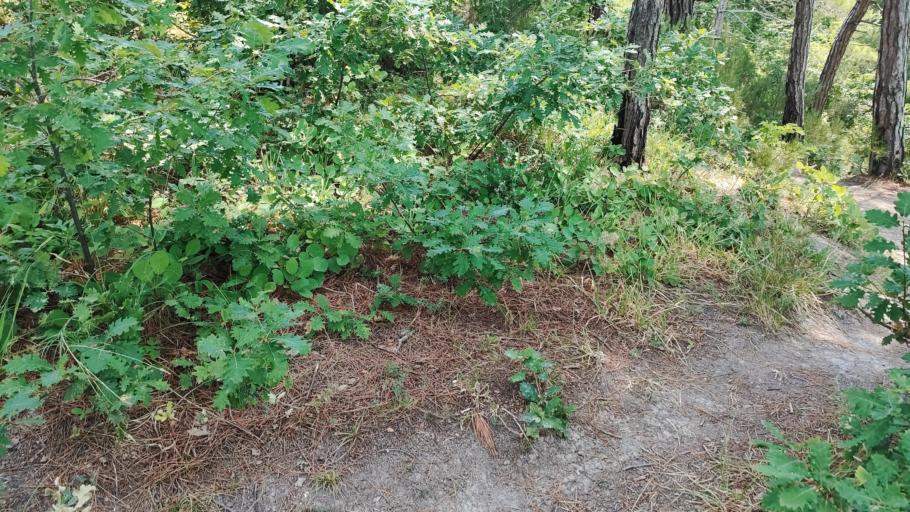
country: RU
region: Krasnodarskiy
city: Divnomorskoye
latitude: 44.4788
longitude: 38.1415
